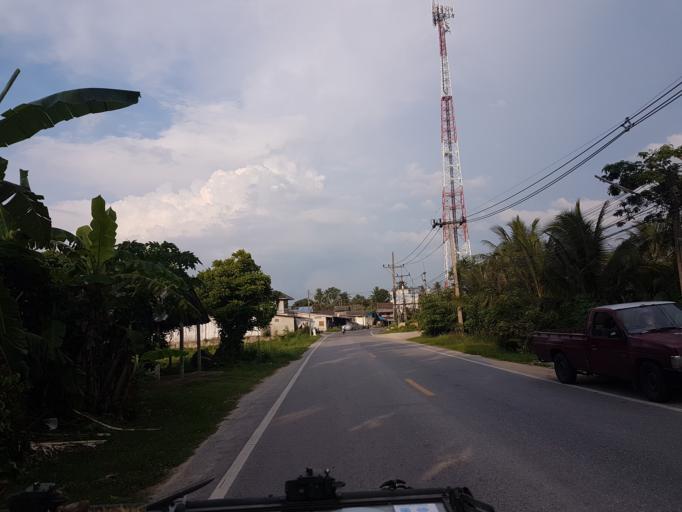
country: TH
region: Pattani
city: Khok Pho
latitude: 6.6753
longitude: 101.1000
